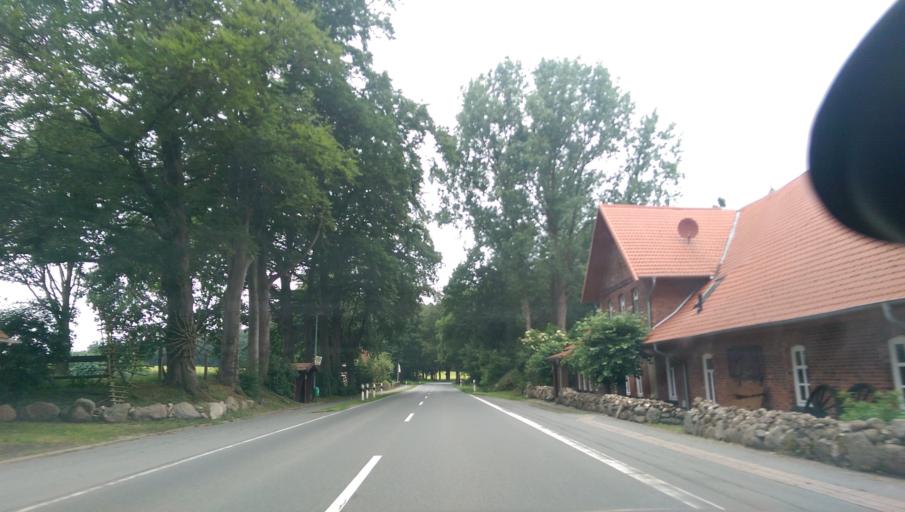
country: DE
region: Lower Saxony
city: Bomlitz
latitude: 52.9321
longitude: 9.6895
